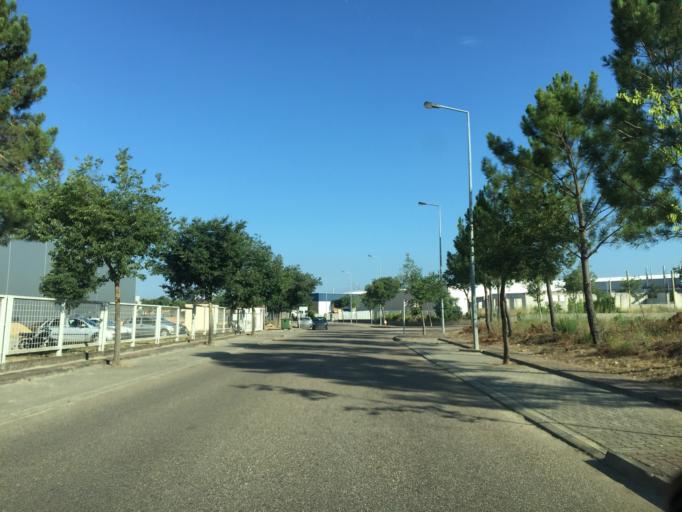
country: PT
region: Santarem
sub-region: Abrantes
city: Alferrarede
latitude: 39.4913
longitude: -8.1855
